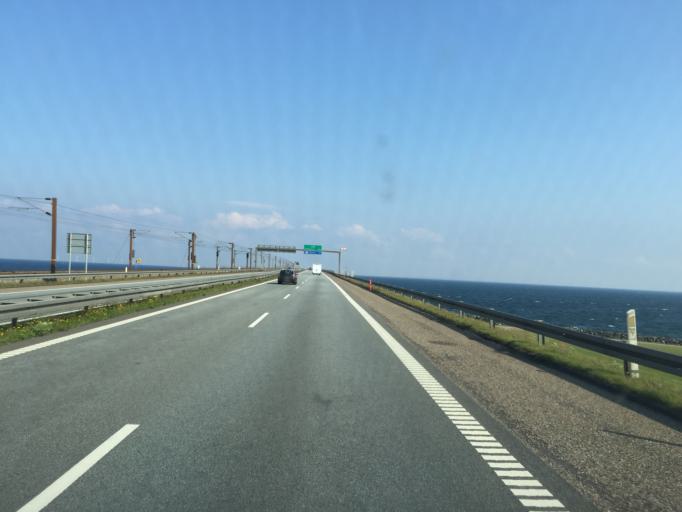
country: DK
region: South Denmark
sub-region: Nyborg Kommune
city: Nyborg
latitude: 55.2989
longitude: 10.8496
